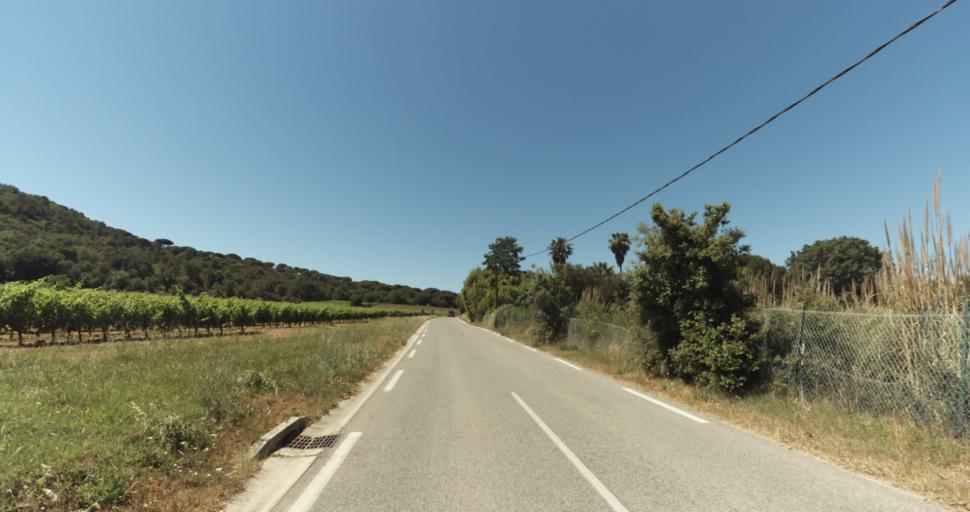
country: FR
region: Provence-Alpes-Cote d'Azur
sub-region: Departement du Var
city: Gassin
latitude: 43.2472
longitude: 6.5784
